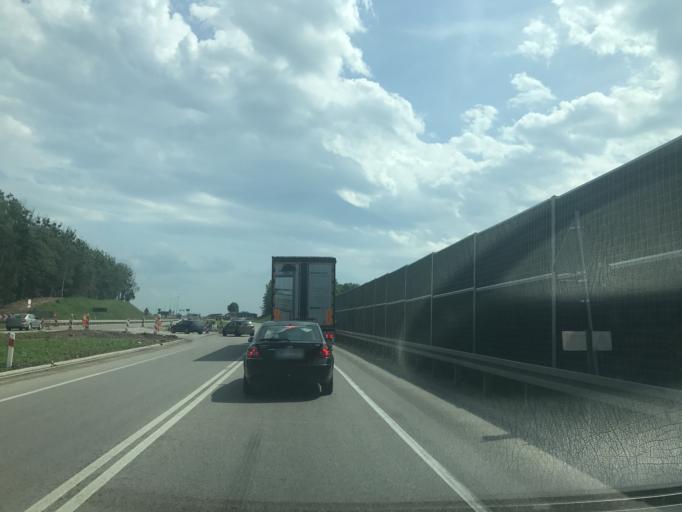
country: PL
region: Warmian-Masurian Voivodeship
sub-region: Powiat ostrodzki
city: Ostroda
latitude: 53.6912
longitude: 19.9885
